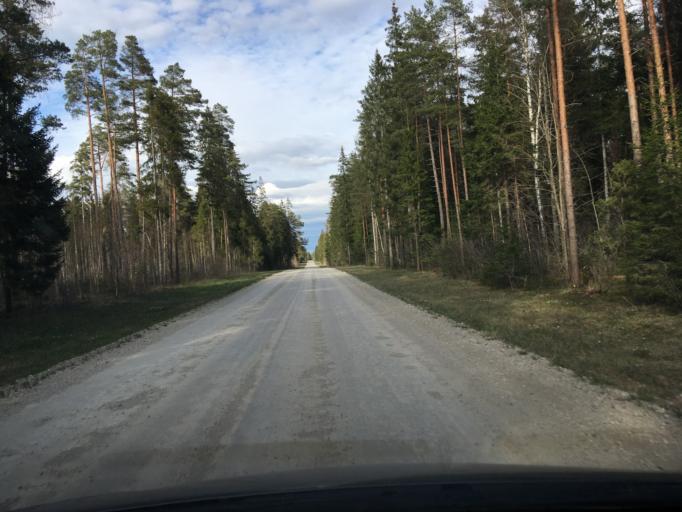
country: EE
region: Raplamaa
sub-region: Maerjamaa vald
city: Marjamaa
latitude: 59.0112
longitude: 24.4043
